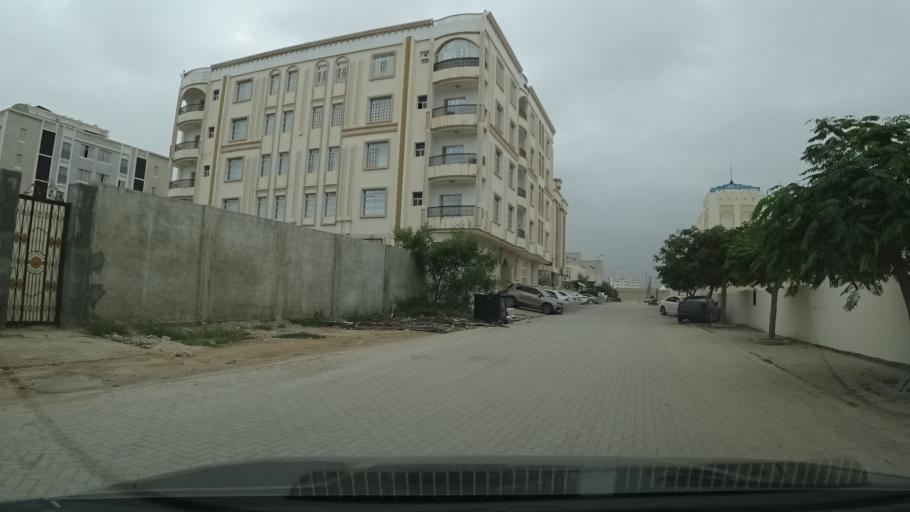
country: OM
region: Zufar
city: Salalah
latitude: 17.0156
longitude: 54.0622
